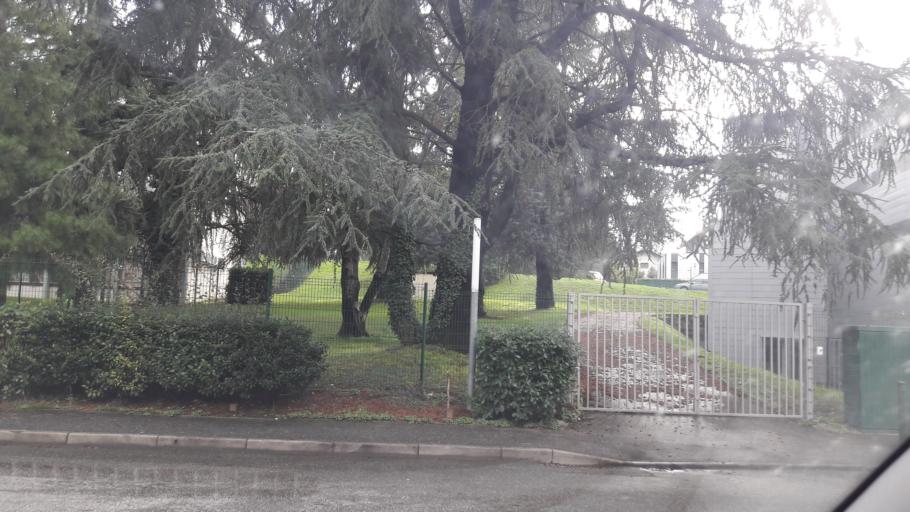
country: FR
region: Rhone-Alpes
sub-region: Departement de la Savoie
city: Montmelian
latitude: 45.5004
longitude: 6.0497
